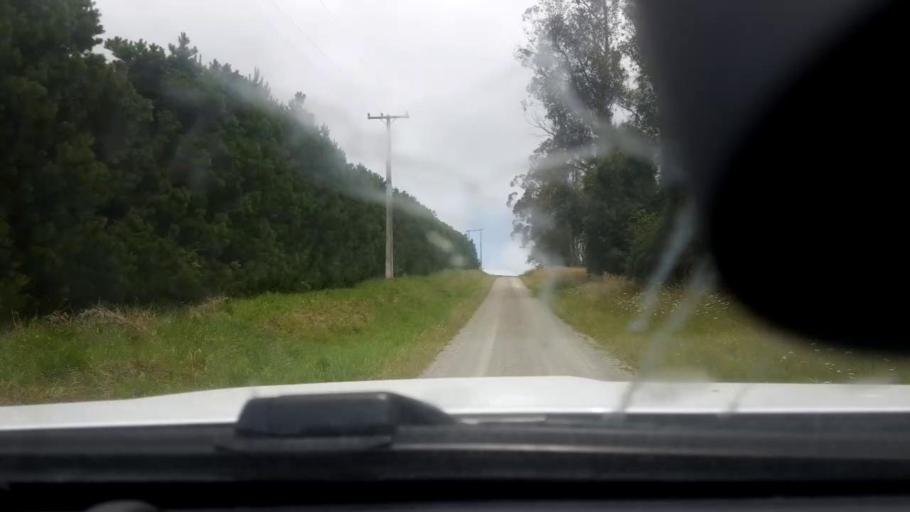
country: NZ
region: Canterbury
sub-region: Timaru District
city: Pleasant Point
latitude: -44.1683
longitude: 171.1459
